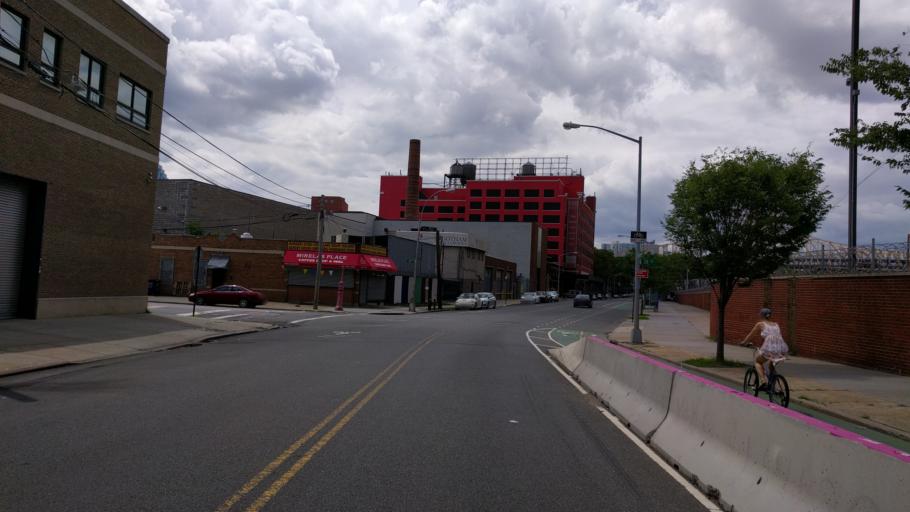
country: US
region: New York
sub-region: Queens County
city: Long Island City
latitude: 40.7596
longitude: -73.9440
